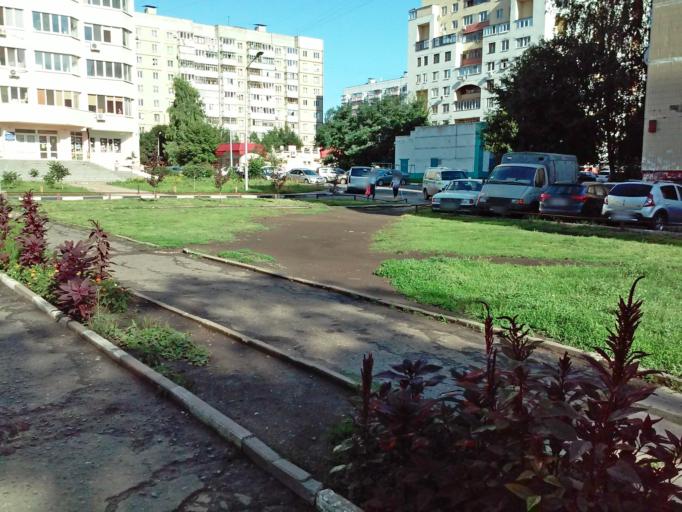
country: RU
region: Belgorod
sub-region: Belgorodskiy Rayon
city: Belgorod
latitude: 50.5589
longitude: 36.5680
